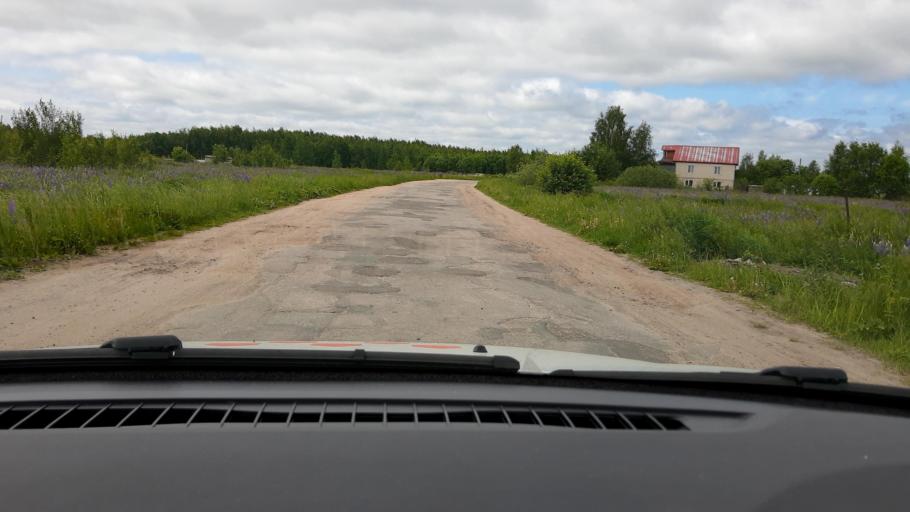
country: RU
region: Nizjnij Novgorod
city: Sitniki
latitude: 56.5188
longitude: 44.1085
